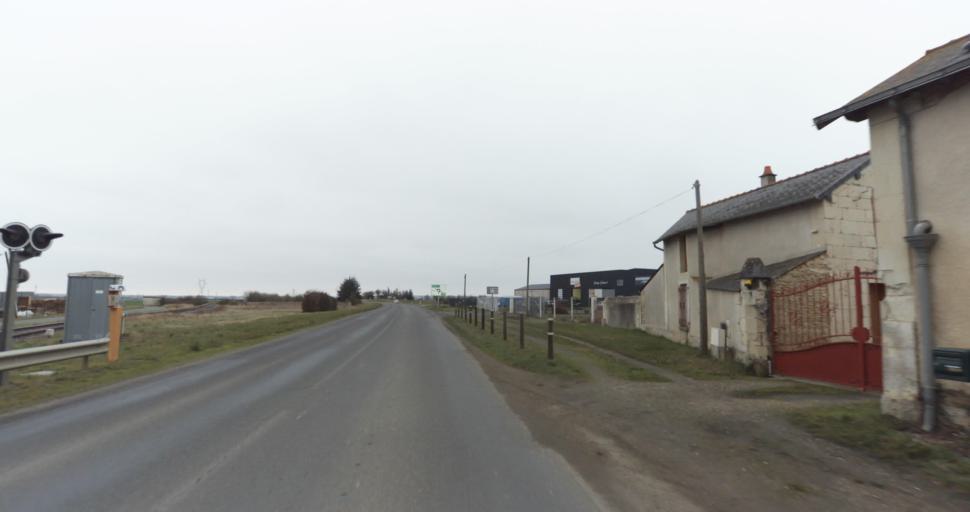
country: FR
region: Pays de la Loire
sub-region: Departement de Maine-et-Loire
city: Montreuil-Bellay
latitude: 47.1200
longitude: -0.1351
